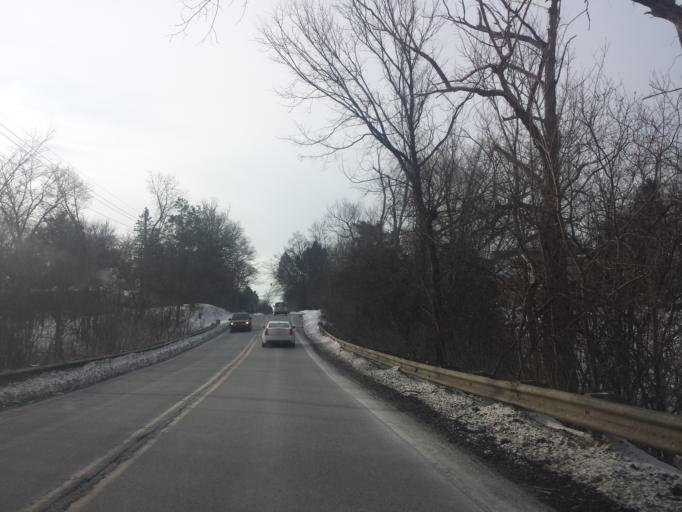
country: US
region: Michigan
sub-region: Oakland County
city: Orchard Lake
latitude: 42.5522
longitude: -83.3415
